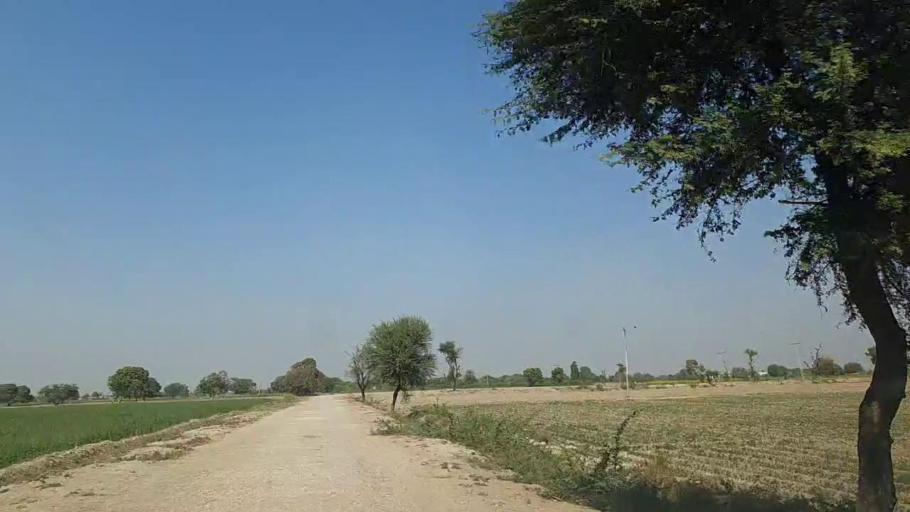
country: PK
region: Sindh
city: Naukot
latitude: 24.8557
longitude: 69.4156
